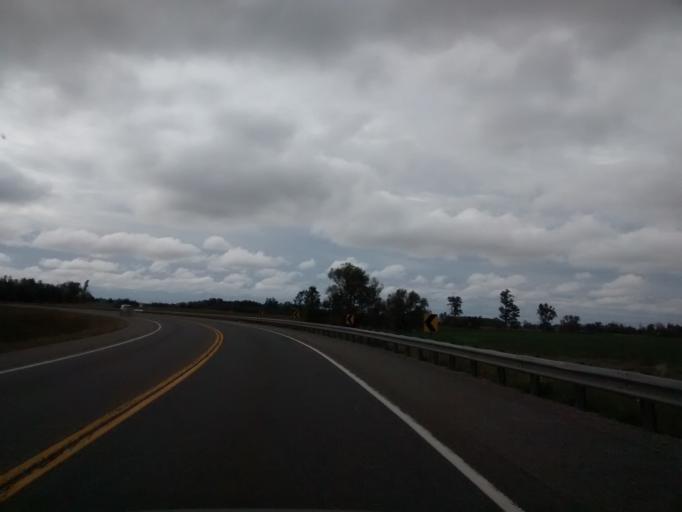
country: CA
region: Ontario
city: Ancaster
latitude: 43.1449
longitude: -79.9276
